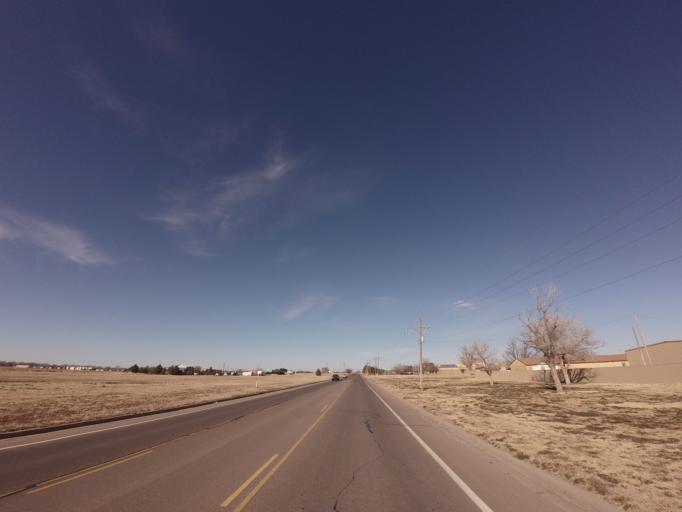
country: US
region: New Mexico
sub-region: Curry County
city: Clovis
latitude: 34.3989
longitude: -103.1683
